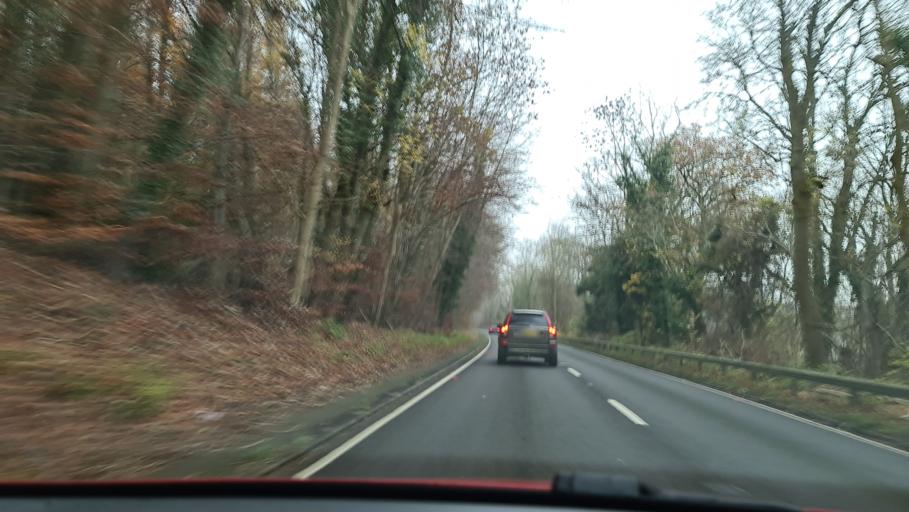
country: GB
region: England
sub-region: Buckinghamshire
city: Stokenchurch
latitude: 51.6452
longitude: -0.8494
